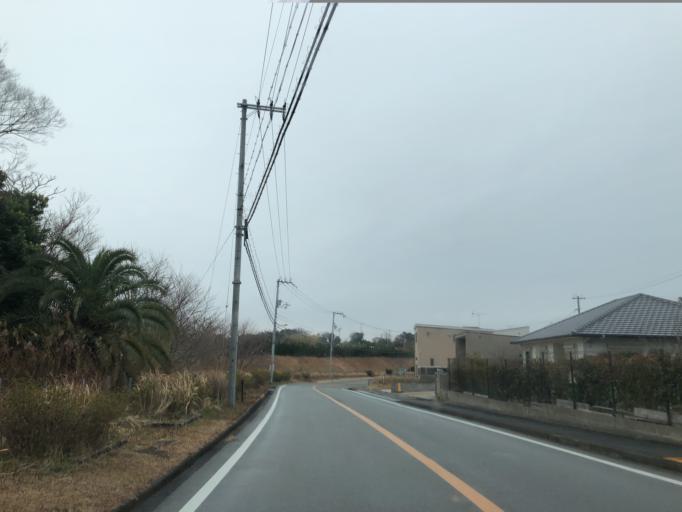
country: JP
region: Wakayama
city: Tanabe
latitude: 33.6645
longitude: 135.3512
